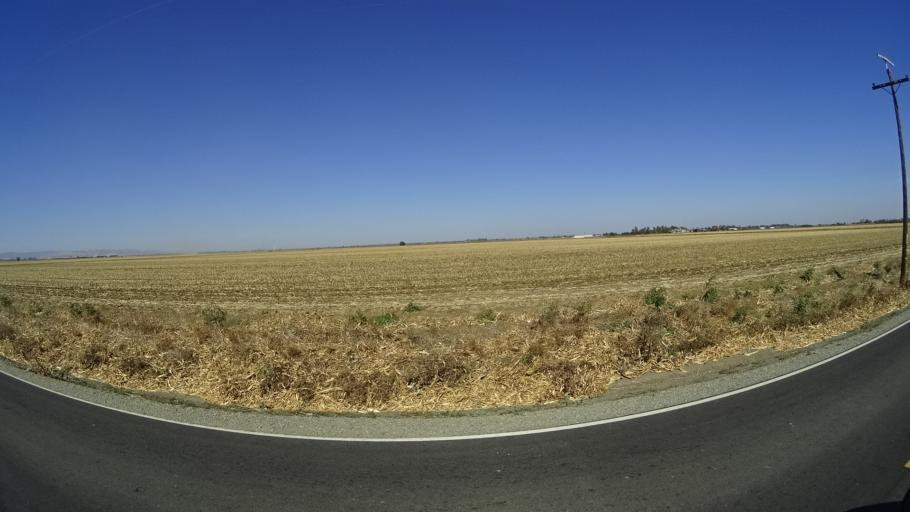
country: US
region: California
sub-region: Yolo County
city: Cottonwood
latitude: 38.6199
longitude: -121.9024
